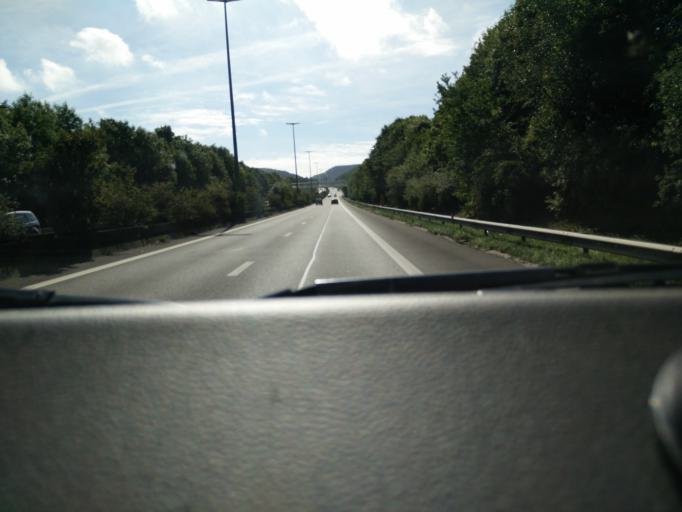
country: BE
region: Wallonia
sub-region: Province du Luxembourg
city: Tellin
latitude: 50.0849
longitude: 5.1659
